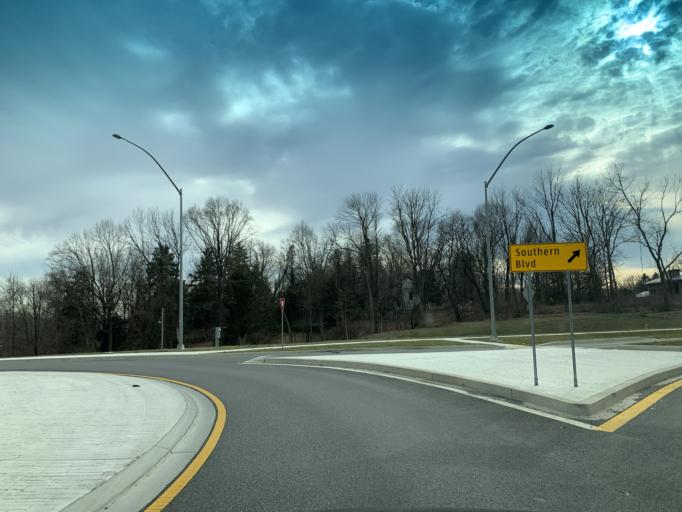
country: US
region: Maryland
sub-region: Washington County
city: Hagerstown
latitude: 39.6151
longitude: -77.7117
